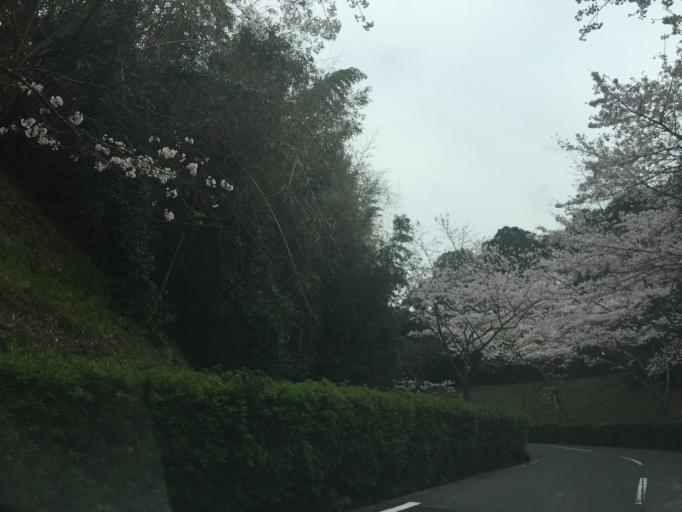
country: JP
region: Shizuoka
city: Mori
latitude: 34.7942
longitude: 137.9686
